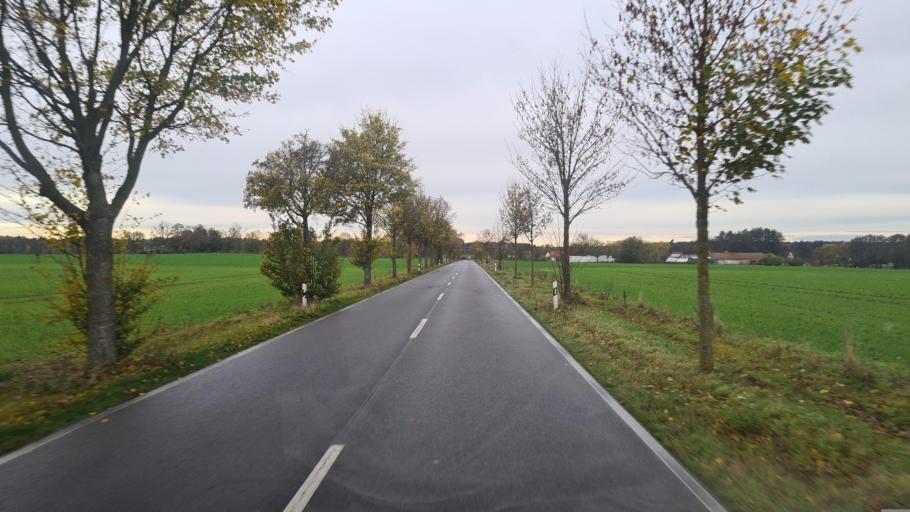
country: DE
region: Saxony-Anhalt
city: Abtsdorf
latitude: 51.9148
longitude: 12.6842
